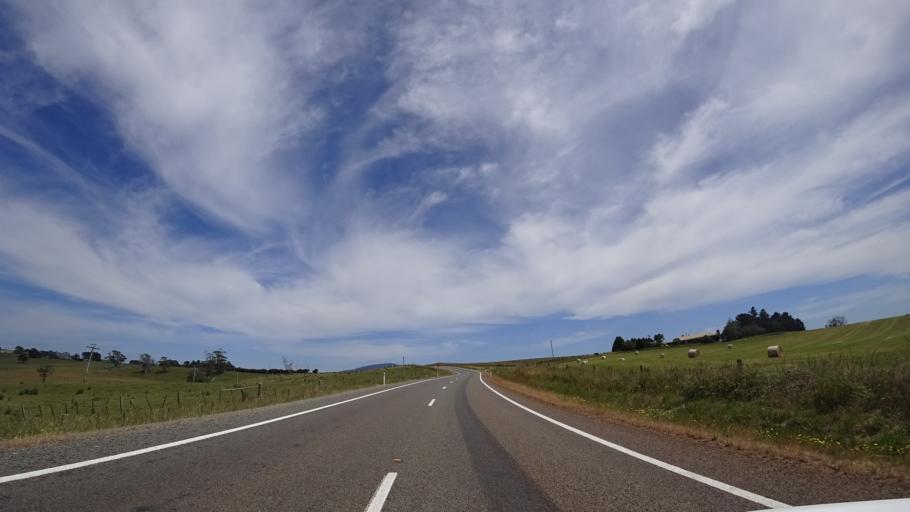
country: AU
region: Tasmania
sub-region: Dorset
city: Scottsdale
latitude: -41.1050
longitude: 147.8511
